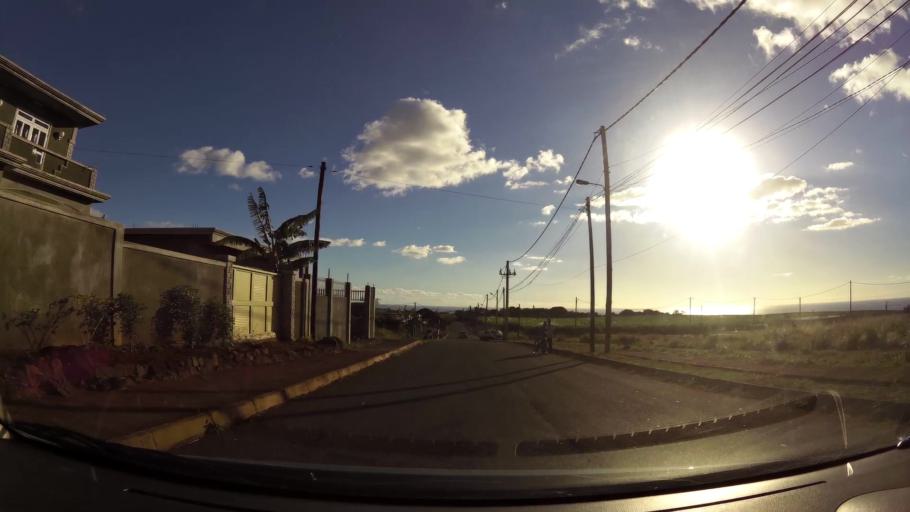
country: MU
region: Black River
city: Petite Riviere
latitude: -20.2146
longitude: 57.4636
